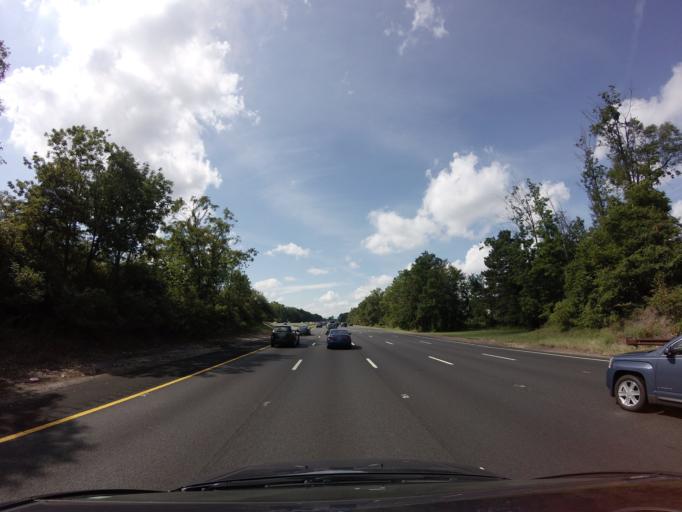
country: US
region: New Jersey
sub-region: Middlesex County
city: Iselin
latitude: 40.5992
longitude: -74.3189
